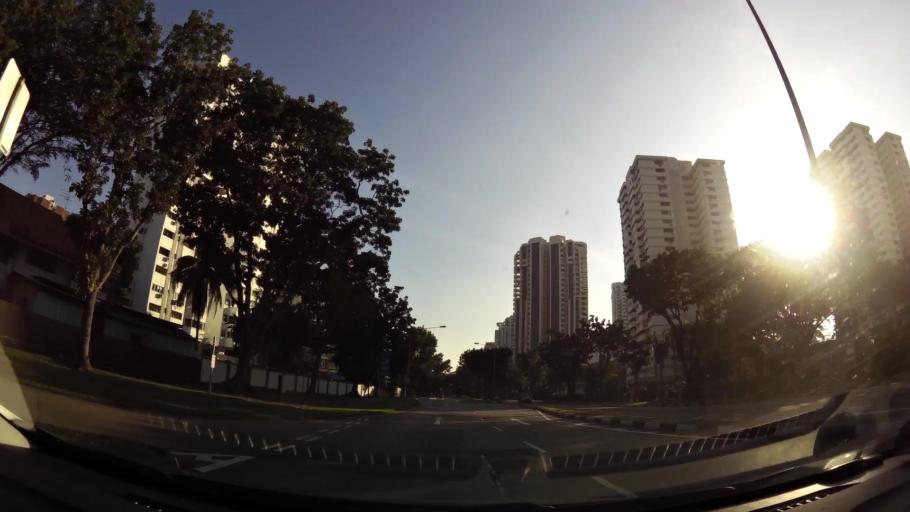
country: SG
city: Singapore
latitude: 1.3109
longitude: 103.9329
